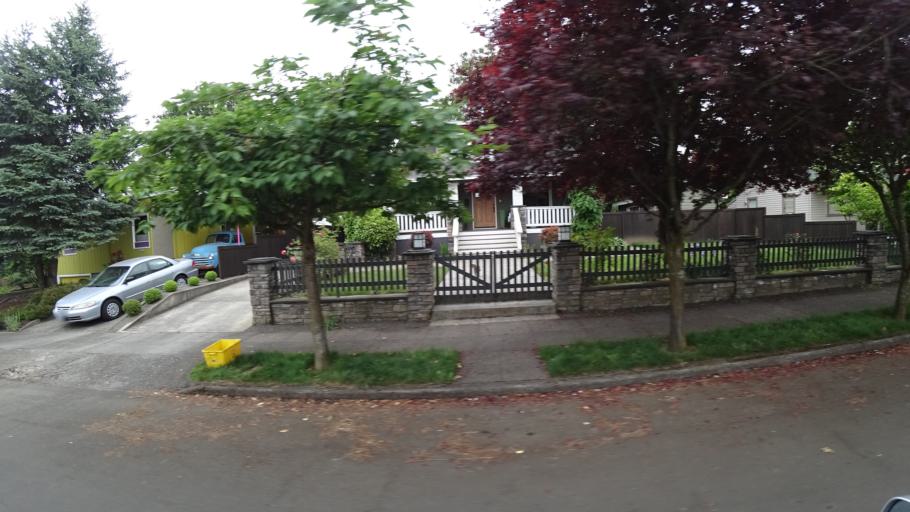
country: US
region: Oregon
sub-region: Multnomah County
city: Portland
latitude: 45.5546
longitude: -122.6192
